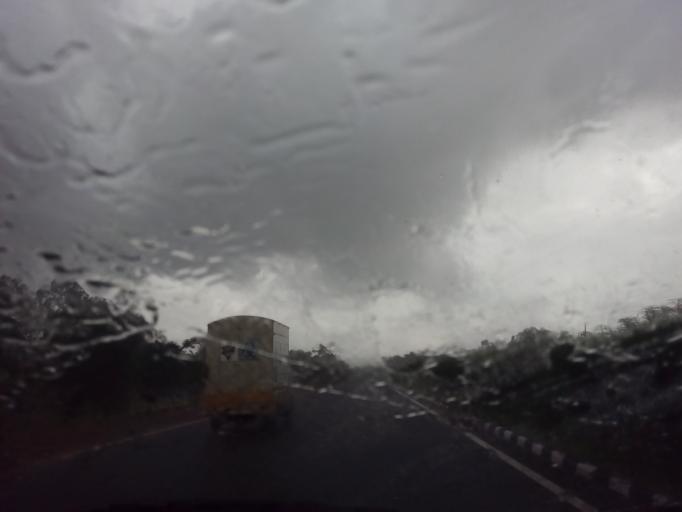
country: IN
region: Karnataka
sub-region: Belgaum
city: Belgaum
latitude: 16.0099
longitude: 74.5145
